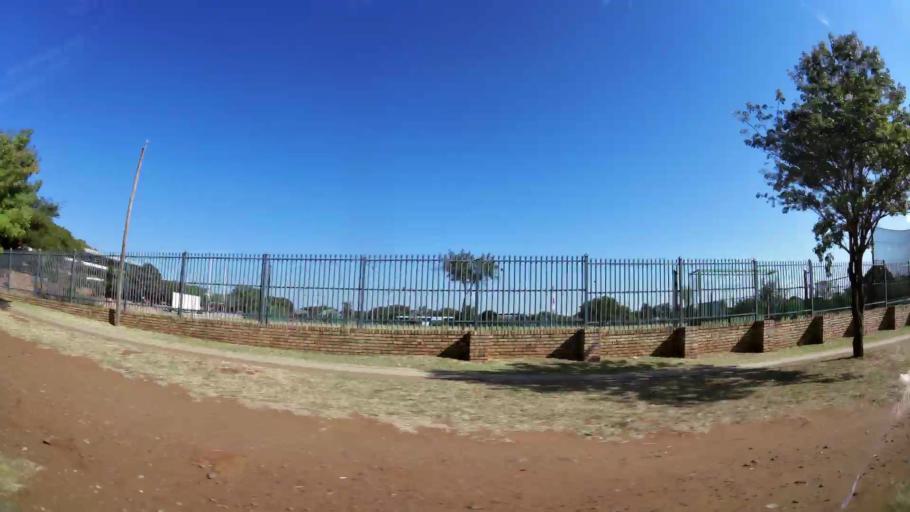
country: ZA
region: Gauteng
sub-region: City of Tshwane Metropolitan Municipality
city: Pretoria
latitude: -25.6721
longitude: 28.2432
